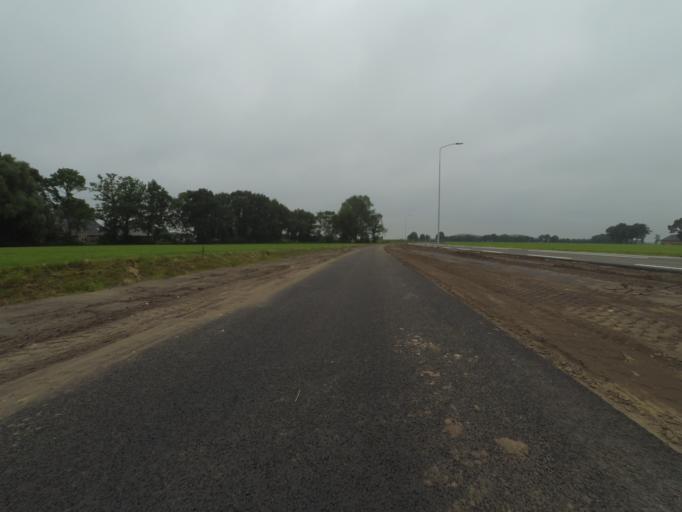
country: NL
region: Gelderland
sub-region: Gemeente Barneveld
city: Voorthuizen
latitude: 52.1506
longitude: 5.6258
